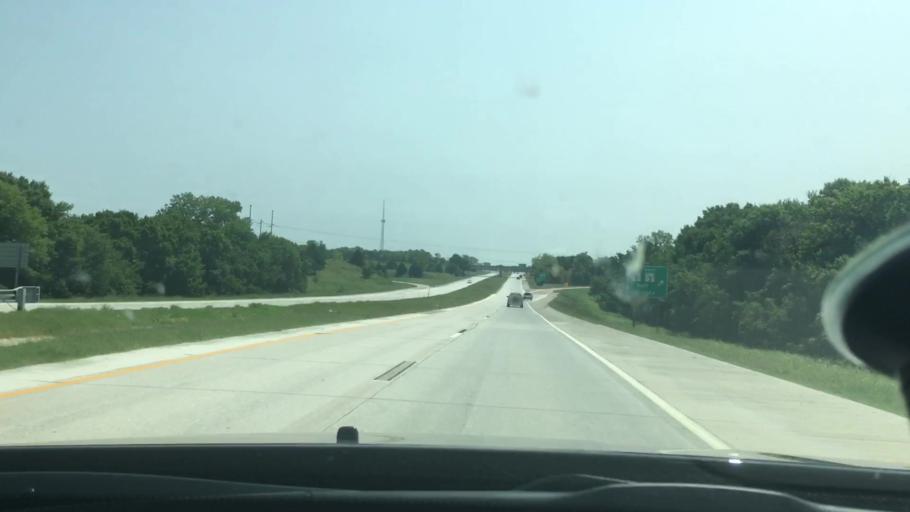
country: US
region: Oklahoma
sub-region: Pontotoc County
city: Ada
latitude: 34.7786
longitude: -96.7084
